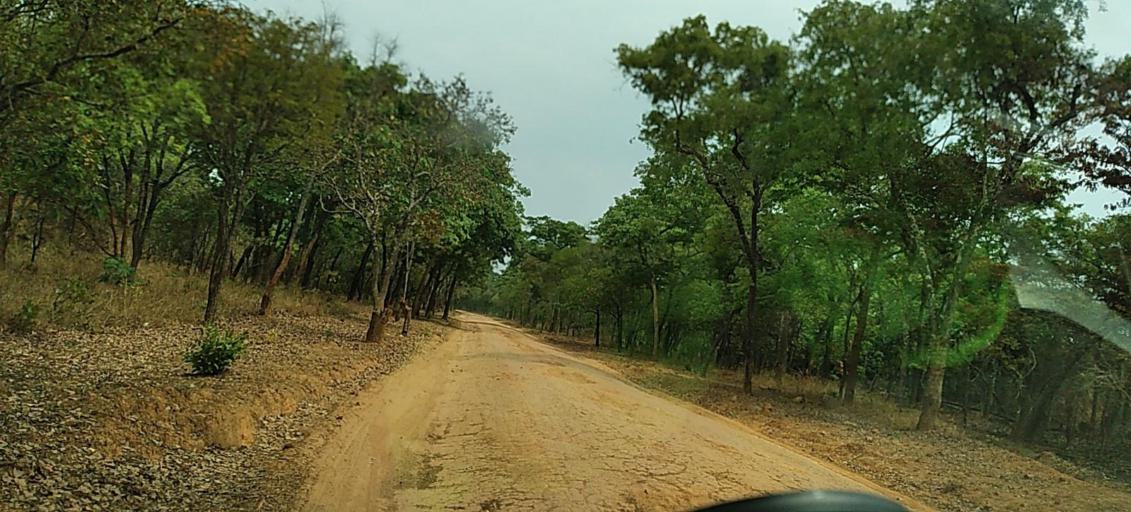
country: ZM
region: North-Western
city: Solwezi
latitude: -12.9435
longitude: 26.5583
